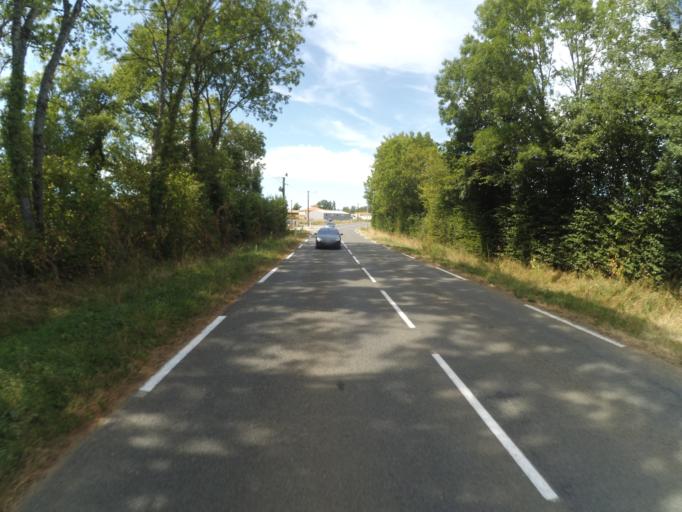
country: FR
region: Poitou-Charentes
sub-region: Departement de la Charente
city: Confolens
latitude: 45.9584
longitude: 0.7027
